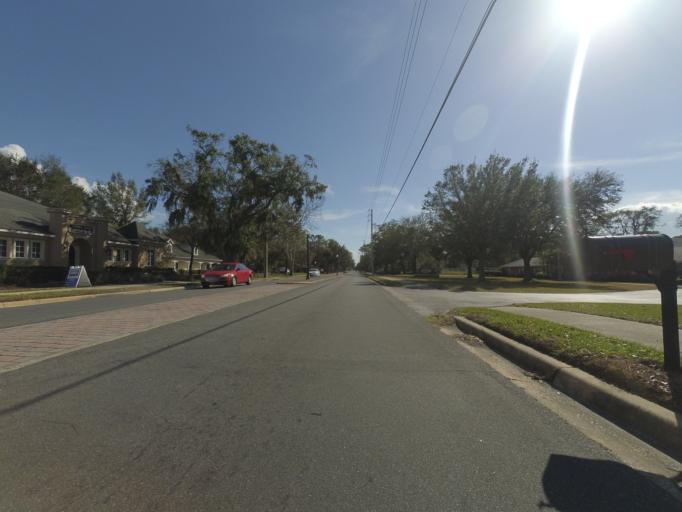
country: US
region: Florida
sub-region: Lake County
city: Mount Dora
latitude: 28.8132
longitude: -81.6449
